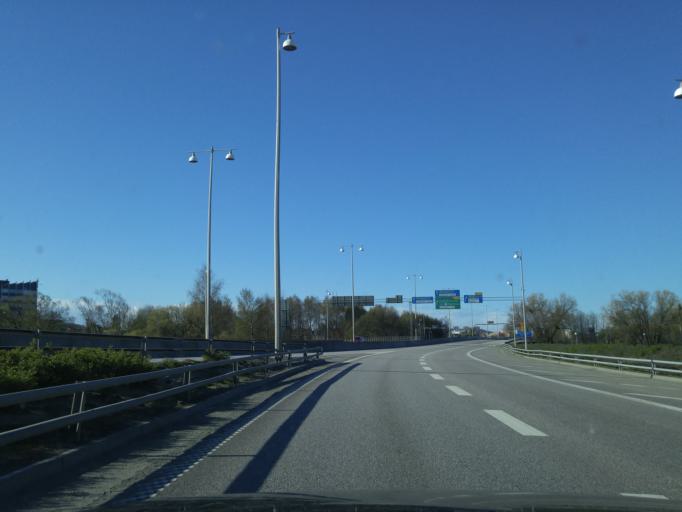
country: SE
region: Vaestra Goetaland
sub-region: Goteborg
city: Goeteborg
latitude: 57.7223
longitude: 11.9964
